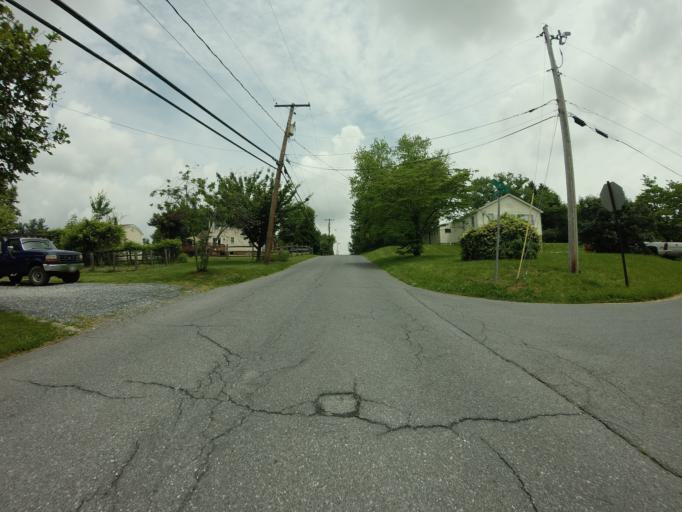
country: US
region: Maryland
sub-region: Frederick County
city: Brunswick
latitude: 39.3176
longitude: -77.6217
